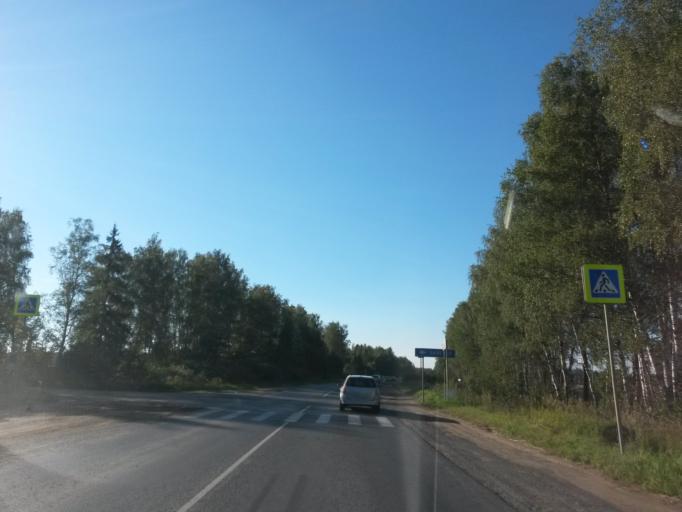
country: RU
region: Ivanovo
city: Novo-Talitsy
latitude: 57.0260
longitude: 40.7591
